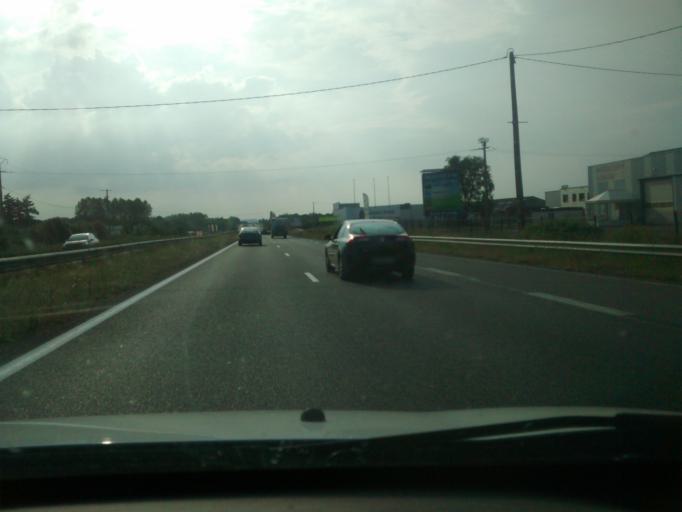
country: FR
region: Brittany
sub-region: Departement des Cotes-d'Armor
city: Saint-Agathon
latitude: 48.5452
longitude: -3.0897
